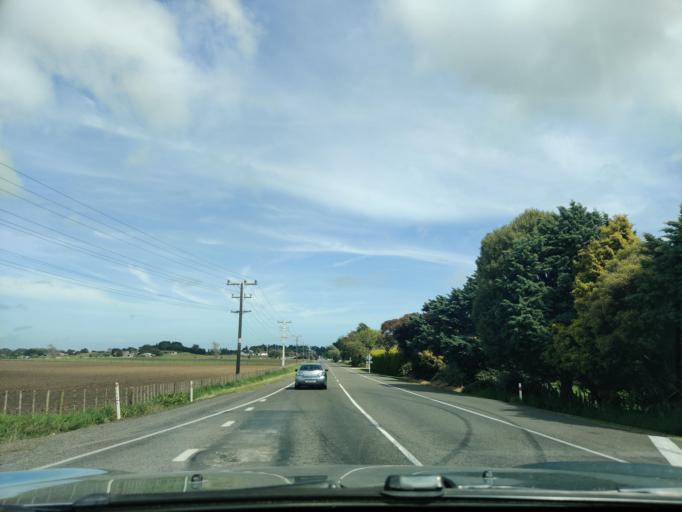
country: NZ
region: Manawatu-Wanganui
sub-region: Wanganui District
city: Wanganui
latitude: -39.8895
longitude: 175.0068
